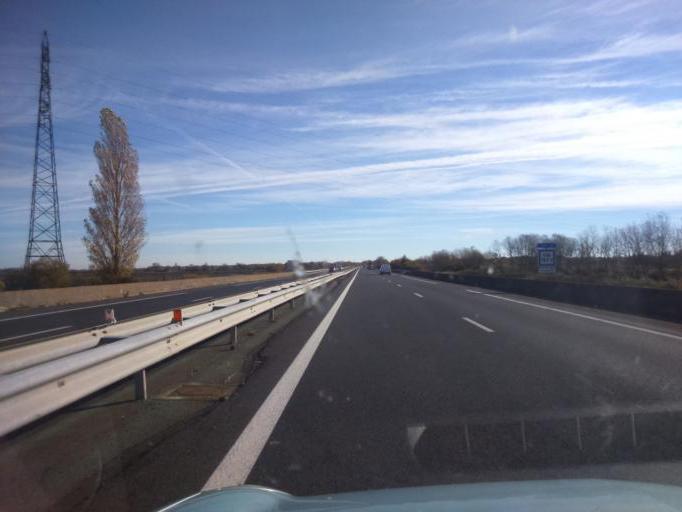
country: FR
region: Poitou-Charentes
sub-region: Departement de la Charente-Maritime
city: Tonnay-Charente
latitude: 45.9574
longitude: -0.9308
